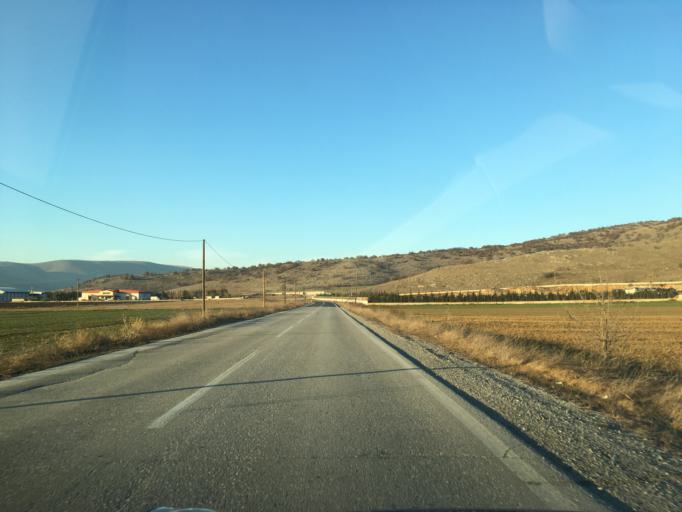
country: GR
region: West Macedonia
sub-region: Nomos Kozanis
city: Kozani
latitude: 40.3001
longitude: 21.7355
